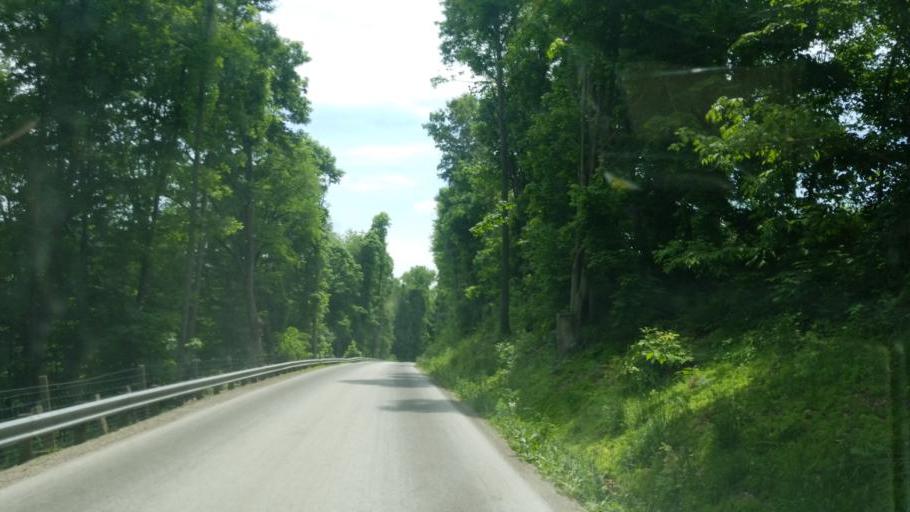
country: US
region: Ohio
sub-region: Coshocton County
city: West Lafayette
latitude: 40.4097
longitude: -81.7710
